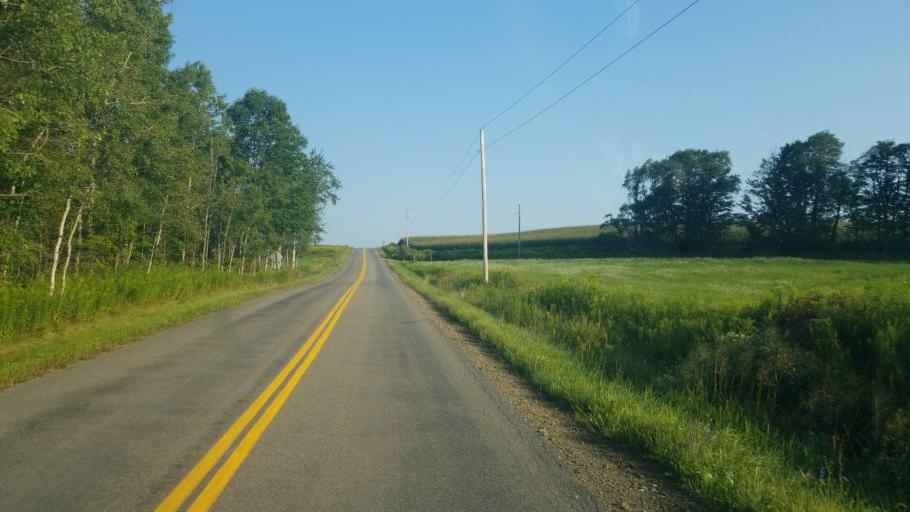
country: US
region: Pennsylvania
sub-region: Tioga County
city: Westfield
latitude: 42.0709
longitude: -77.6352
